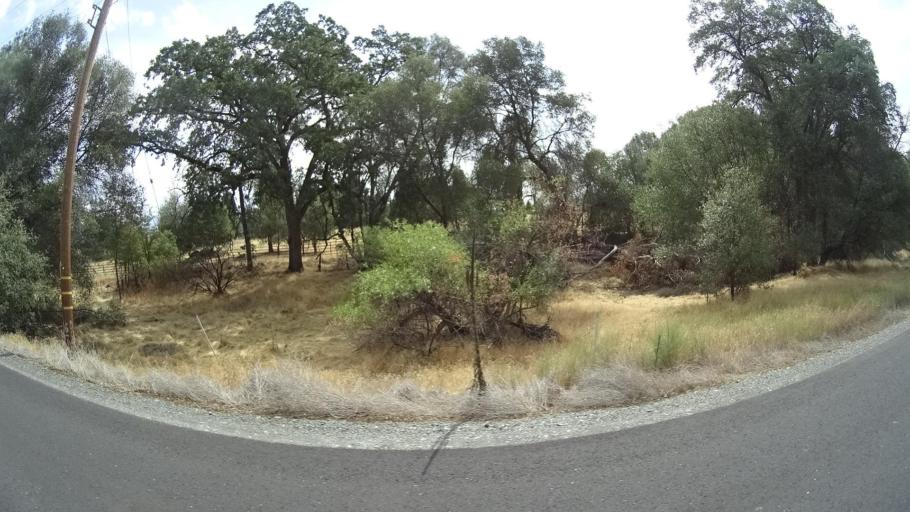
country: US
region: California
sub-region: Mariposa County
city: Mariposa
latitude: 37.4705
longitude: -119.8999
